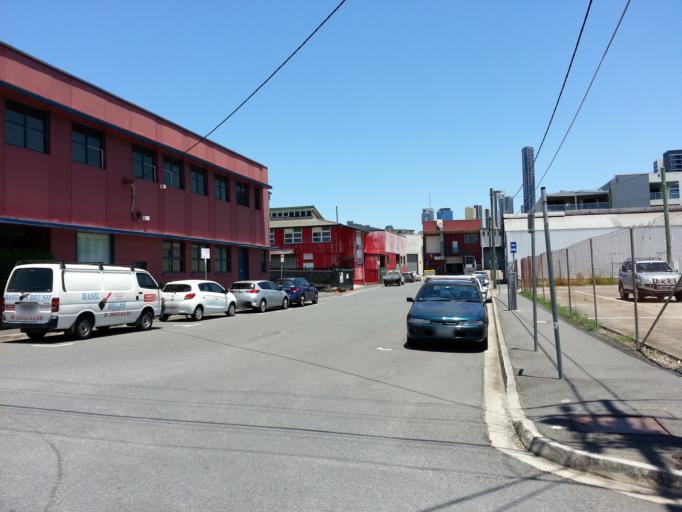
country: AU
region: Queensland
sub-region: Brisbane
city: Fortitude Valley
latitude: -27.4547
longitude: 153.0414
